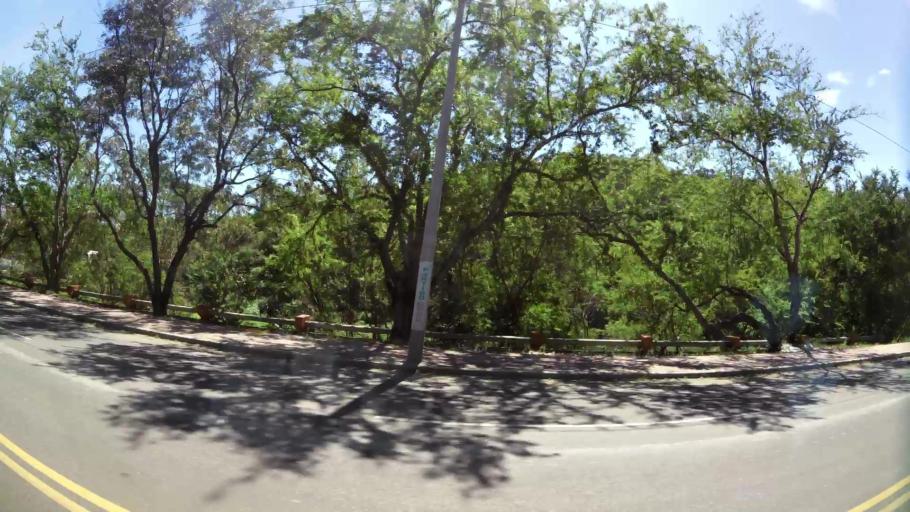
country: DO
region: Santiago
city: Santiago de los Caballeros
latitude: 19.4491
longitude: -70.7126
